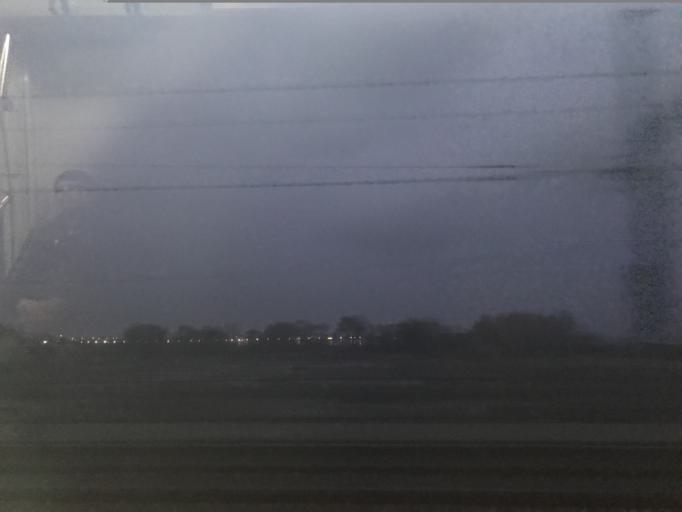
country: TR
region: Istanbul
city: Icmeler
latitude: 40.8109
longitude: 29.3452
